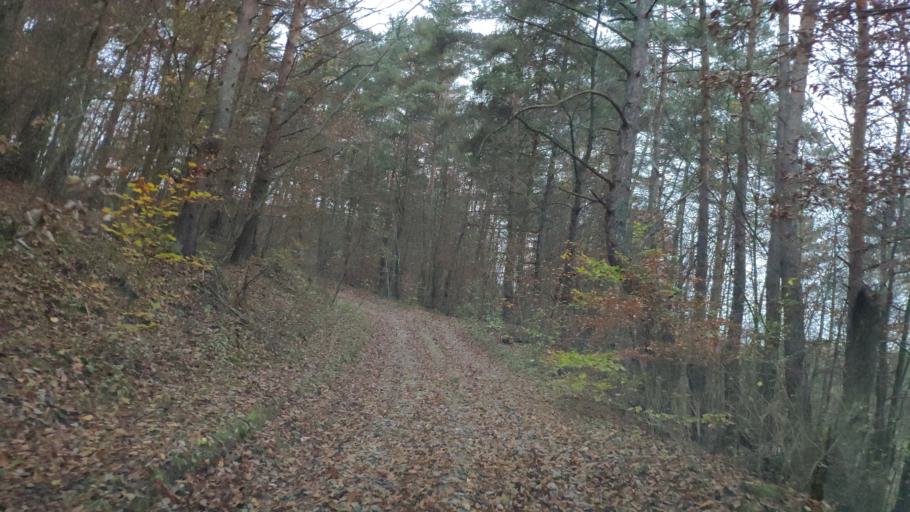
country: SK
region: Presovsky
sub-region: Okres Presov
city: Presov
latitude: 48.9318
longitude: 21.1027
